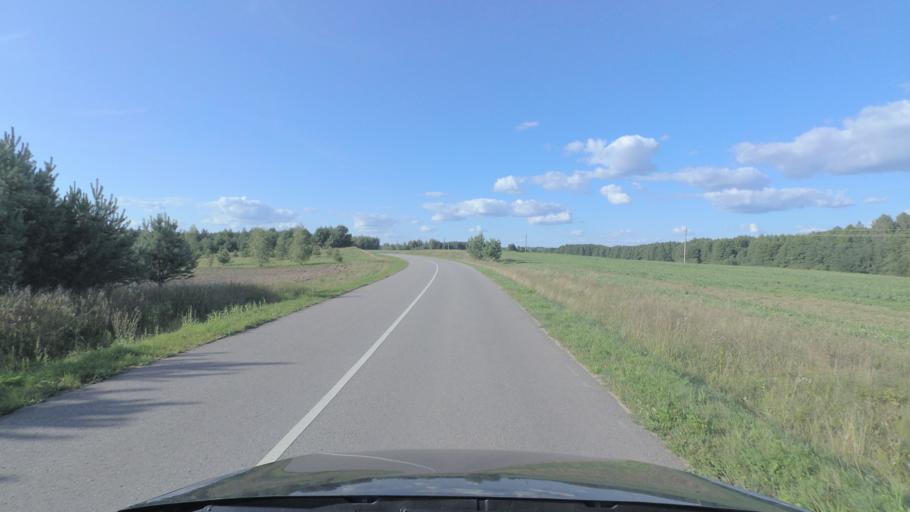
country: LT
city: Pabrade
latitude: 55.0902
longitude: 25.6863
